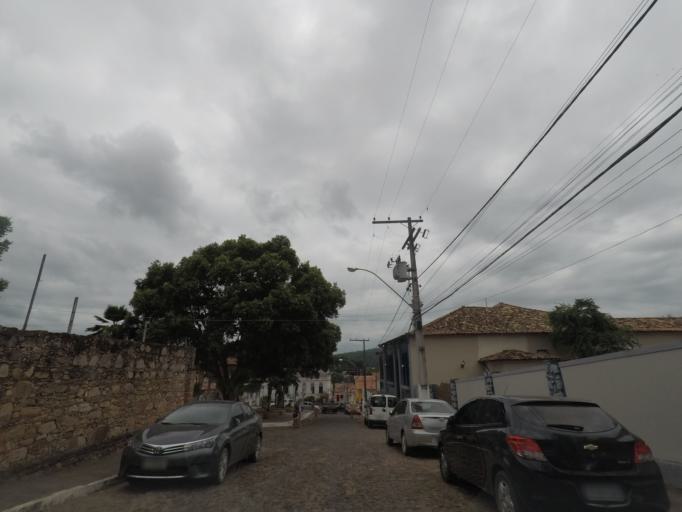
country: BR
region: Bahia
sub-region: Andarai
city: Vera Cruz
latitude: -12.5635
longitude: -41.3914
